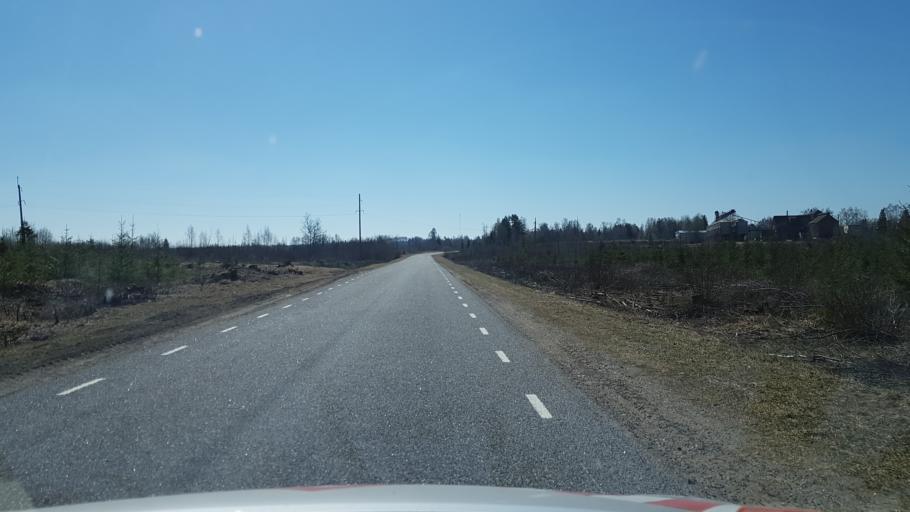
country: EE
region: Laeaene-Virumaa
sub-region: Rakke vald
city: Rakke
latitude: 58.9961
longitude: 26.2734
